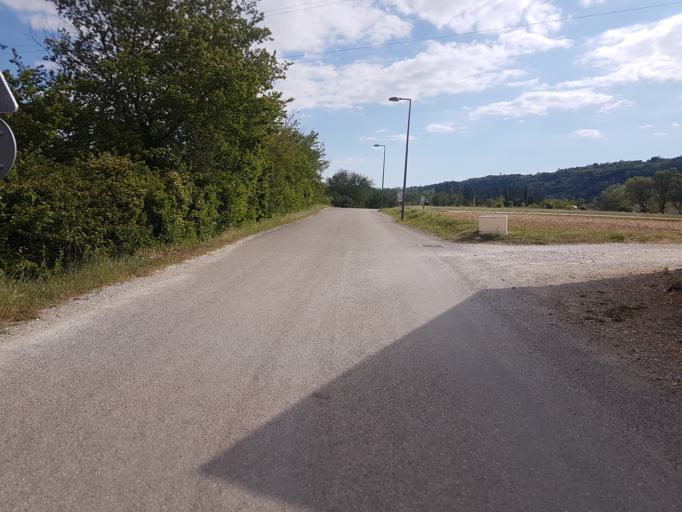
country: FR
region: Rhone-Alpes
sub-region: Departement de l'Ardeche
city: Guilherand-Granges
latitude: 44.9182
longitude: 4.8653
